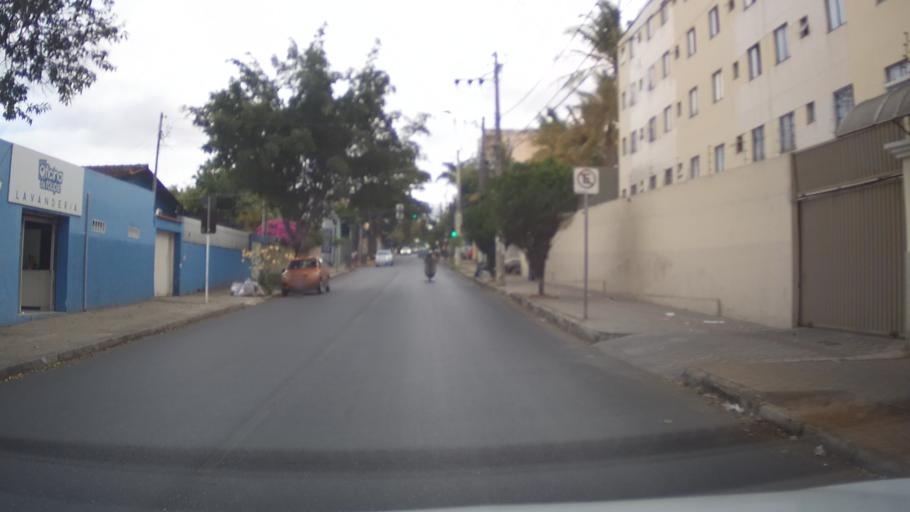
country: BR
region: Minas Gerais
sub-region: Belo Horizonte
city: Belo Horizonte
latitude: -19.8423
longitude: -43.9537
